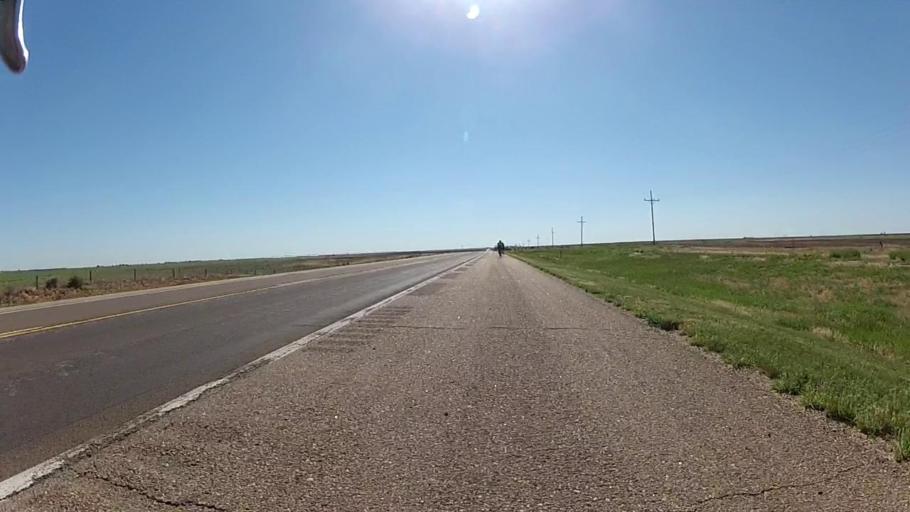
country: US
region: Kansas
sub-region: Kiowa County
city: Greensburg
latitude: 37.5862
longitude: -99.5507
